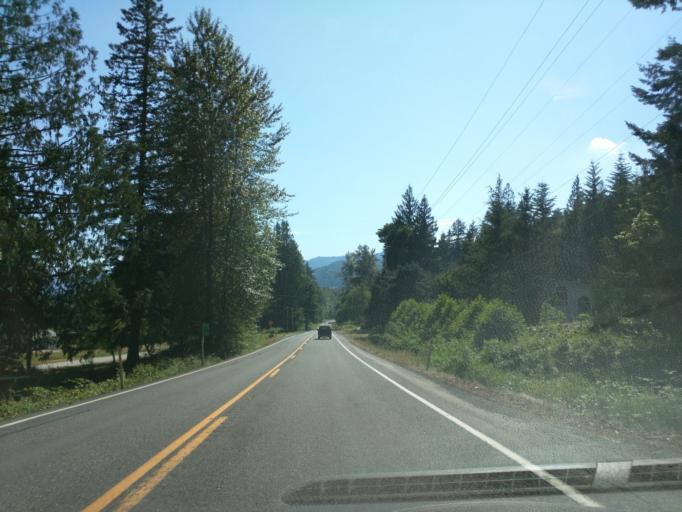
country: US
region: Washington
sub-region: Whatcom County
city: Peaceful Valley
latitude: 48.8281
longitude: -122.1778
